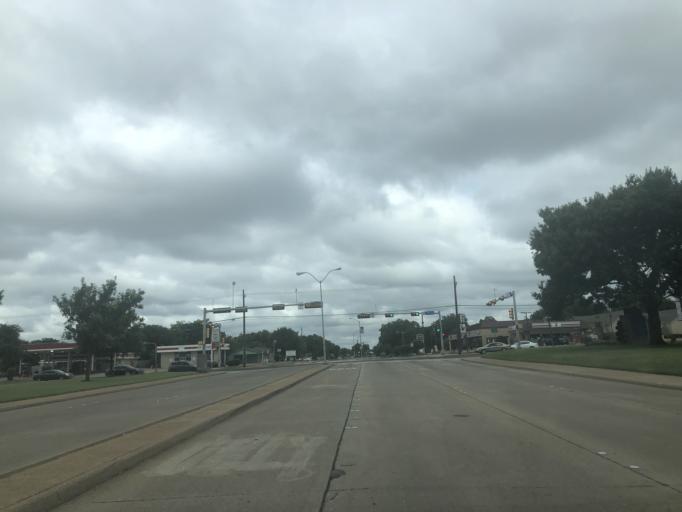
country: US
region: Texas
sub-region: Dallas County
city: Duncanville
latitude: 32.6461
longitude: -96.9054
